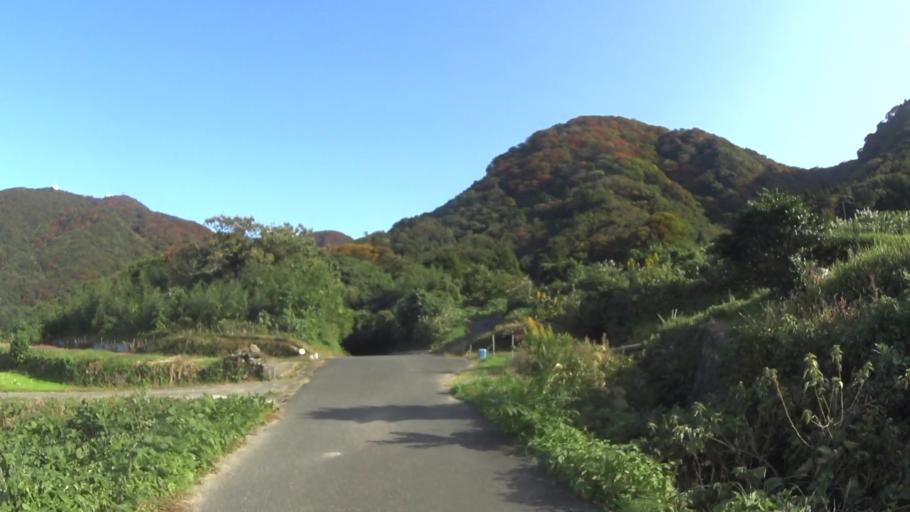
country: JP
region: Kyoto
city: Miyazu
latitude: 35.7612
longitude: 135.2033
